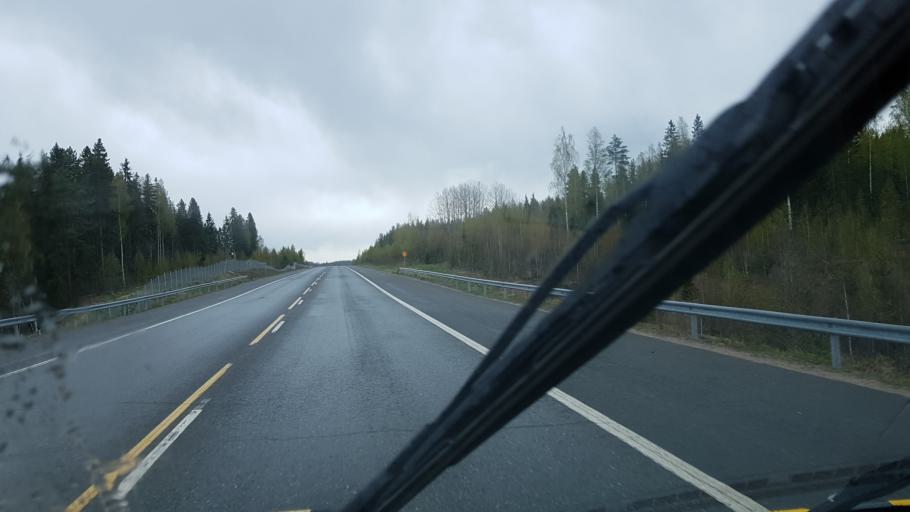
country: FI
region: Pirkanmaa
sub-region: Tampere
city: Pirkkala
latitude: 61.4108
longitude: 23.6340
